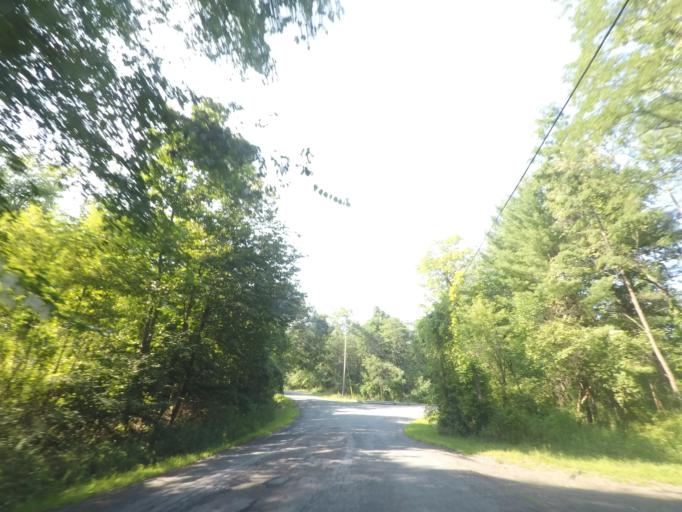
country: US
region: New York
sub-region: Rensselaer County
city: Nassau
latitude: 42.5271
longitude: -73.5678
